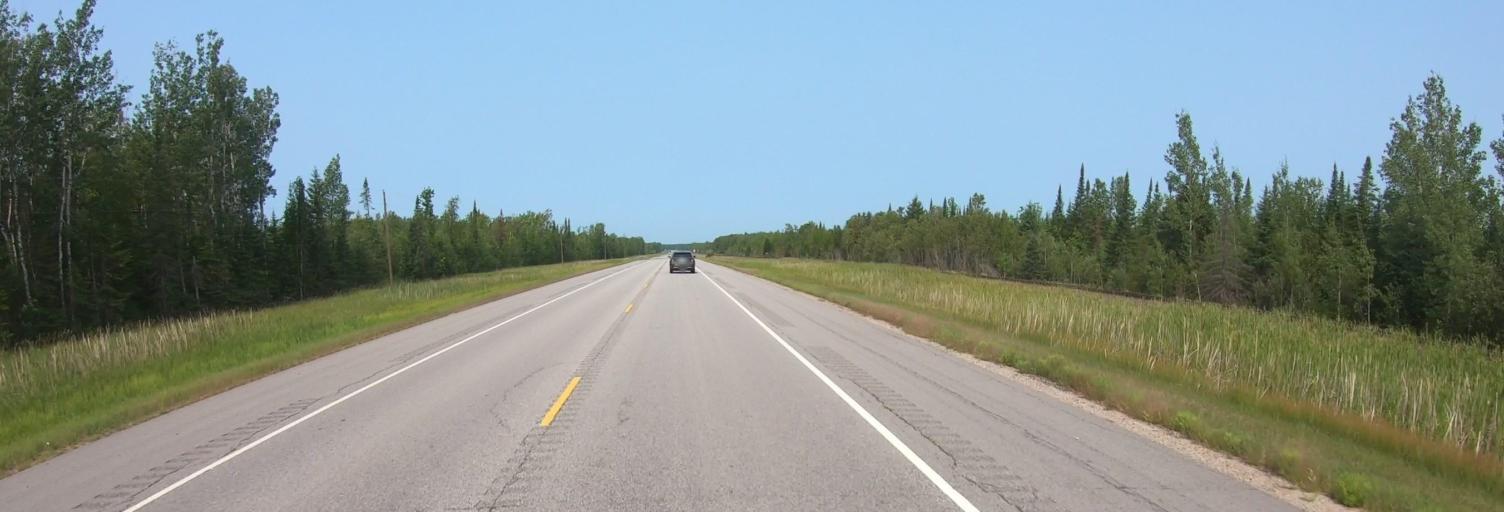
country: CA
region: Ontario
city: Fort Frances
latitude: 48.4702
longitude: -93.3007
